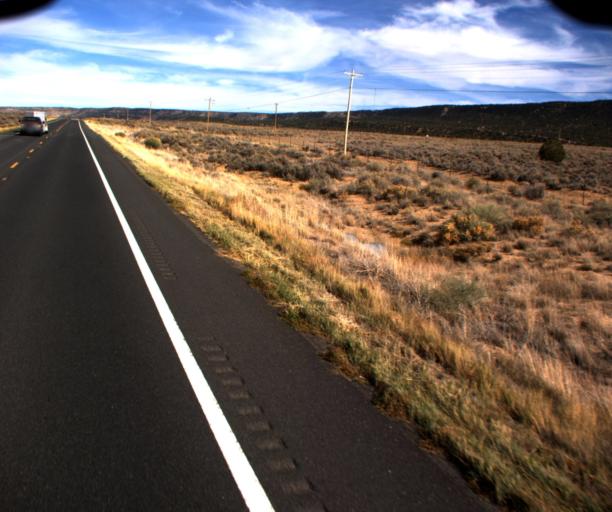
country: US
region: Arizona
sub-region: Navajo County
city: Kayenta
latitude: 36.5434
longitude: -110.5433
